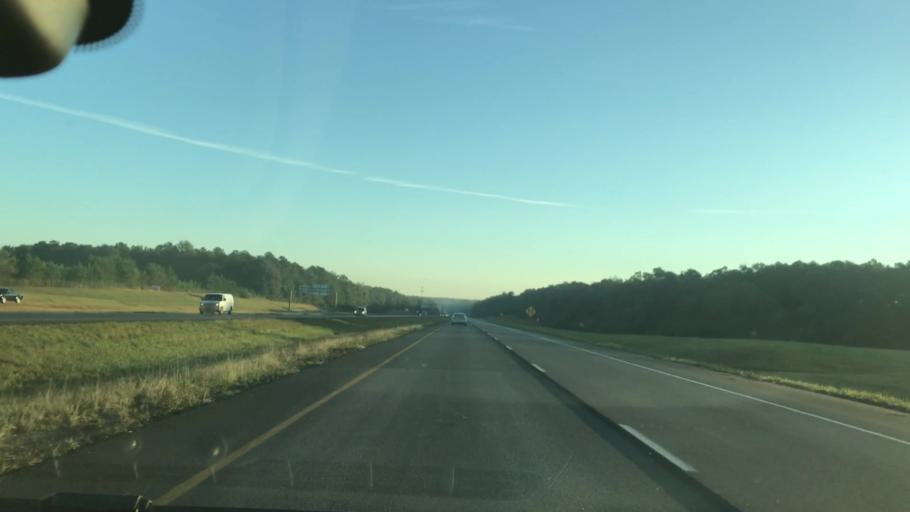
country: US
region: Alabama
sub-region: Mobile County
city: Theodore
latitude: 30.5375
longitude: -88.2389
